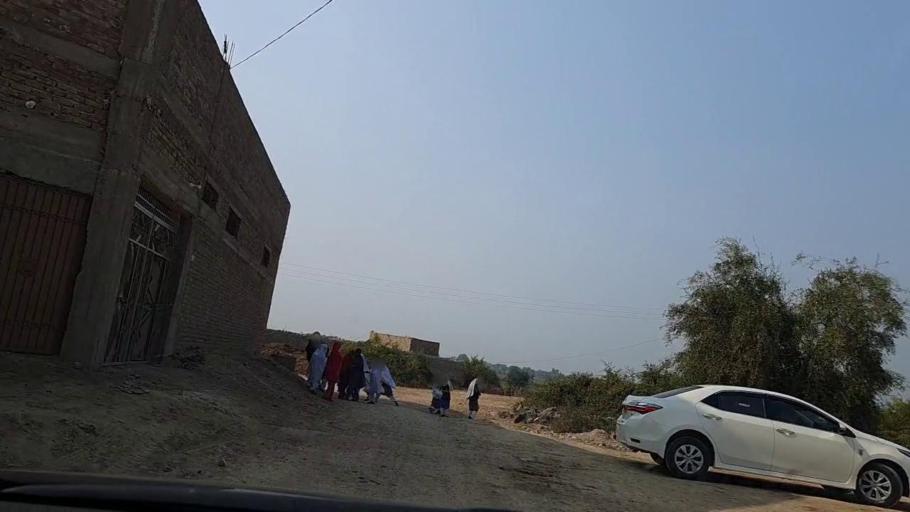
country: PK
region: Sindh
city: Sakrand
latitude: 26.1526
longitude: 68.2487
